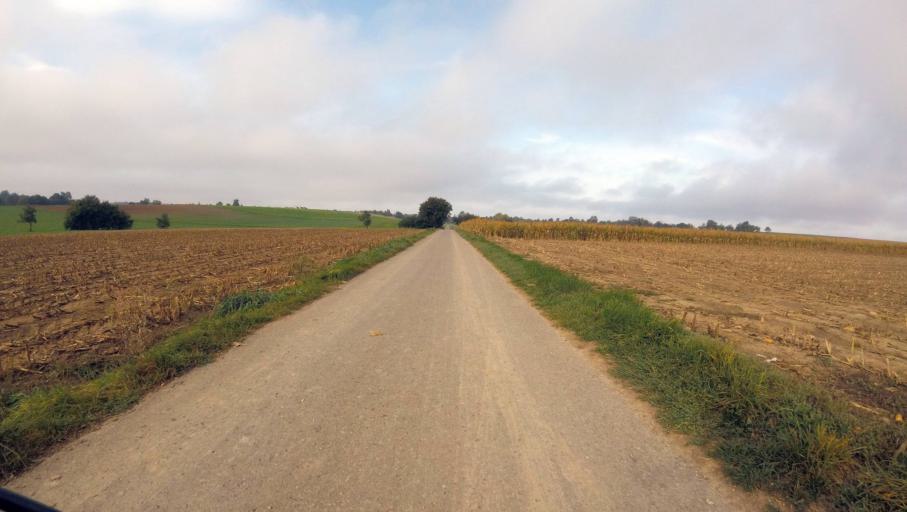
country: DE
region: Baden-Wuerttemberg
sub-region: Regierungsbezirk Stuttgart
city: Motzingen
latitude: 48.5344
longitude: 8.7965
